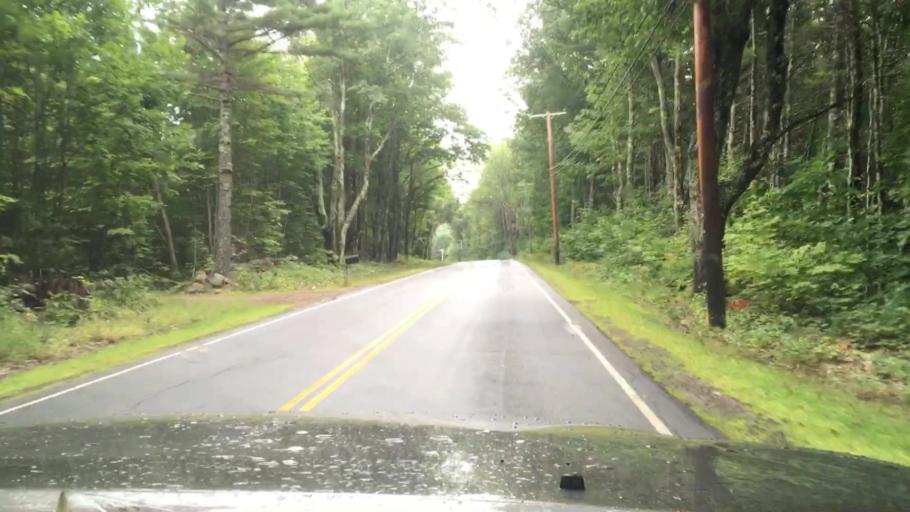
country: US
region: New Hampshire
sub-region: Belknap County
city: Meredith
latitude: 43.6427
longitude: -71.5337
